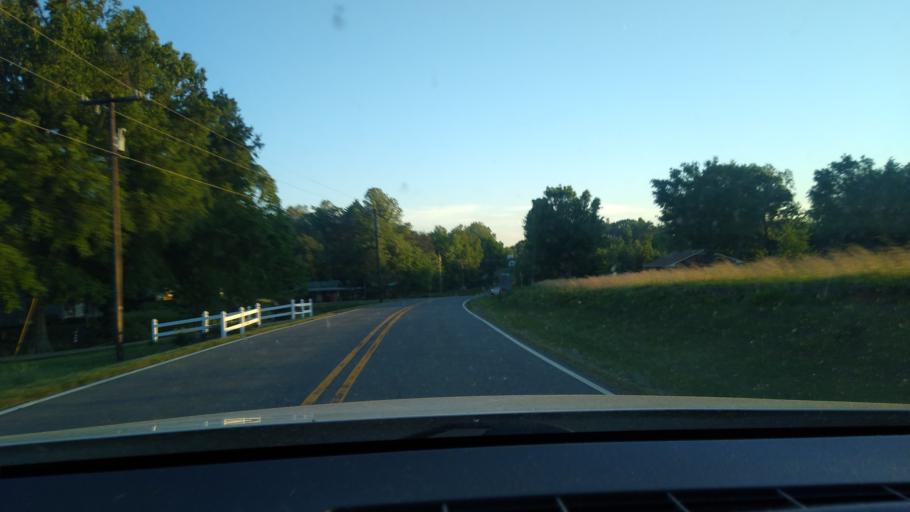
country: US
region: North Carolina
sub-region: Rockingham County
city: Reidsville
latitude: 36.3447
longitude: -79.5722
